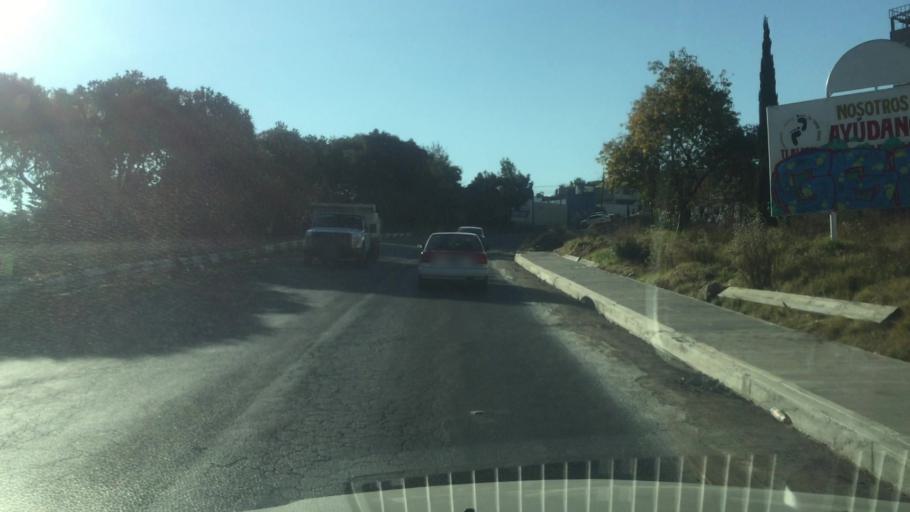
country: MX
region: Mexico City
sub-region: Tlalpan
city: Lomas de Tepemecatl
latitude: 19.2672
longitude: -99.2048
